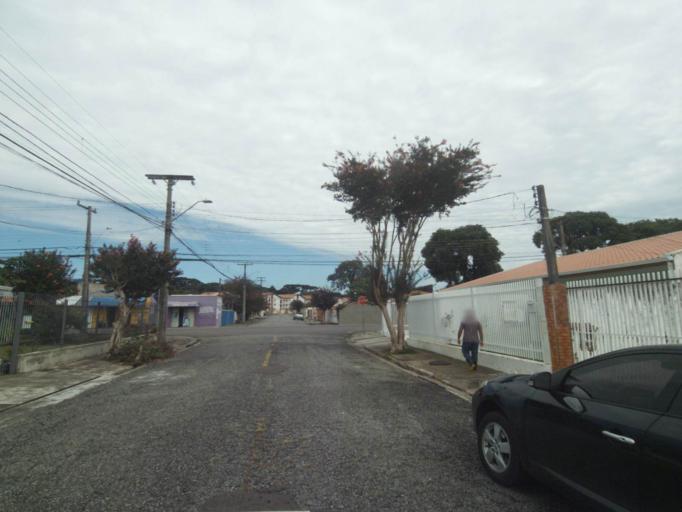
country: BR
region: Parana
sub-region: Pinhais
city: Pinhais
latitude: -25.4716
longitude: -49.1998
